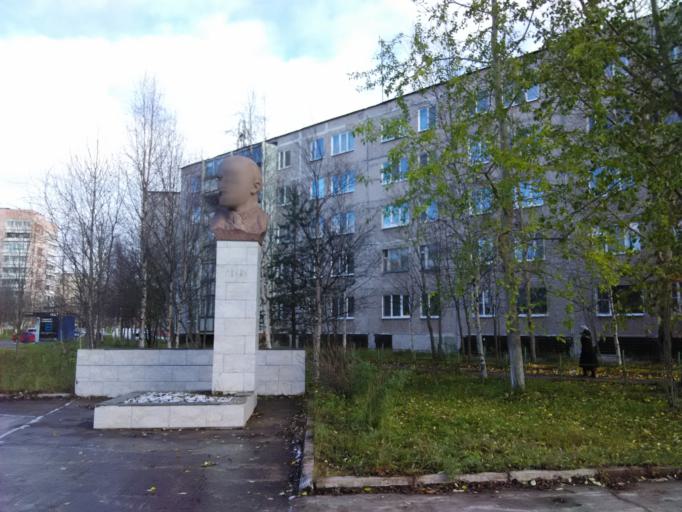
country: RU
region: Murmansk
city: Polyarnyye Zori
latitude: 67.3685
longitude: 32.4892
